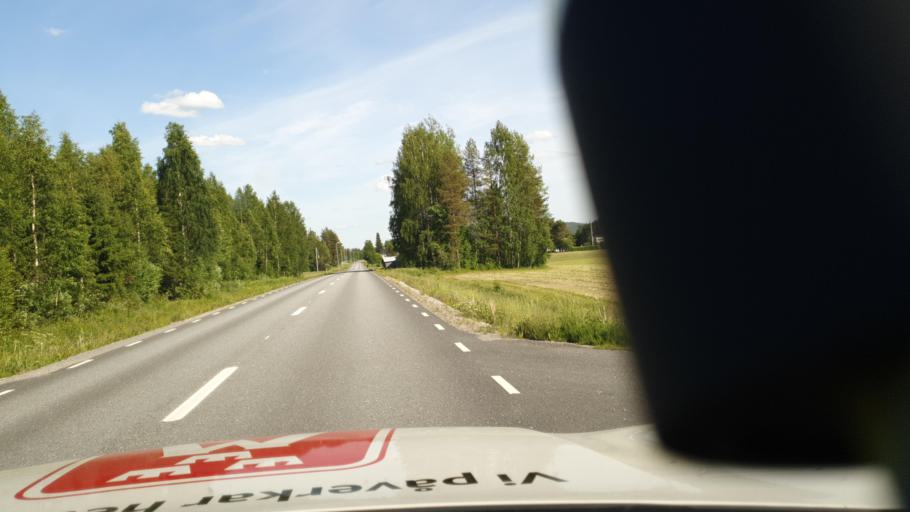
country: SE
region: Vaesterbotten
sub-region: Skelleftea Kommun
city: Forsbacka
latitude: 64.7013
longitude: 20.4598
